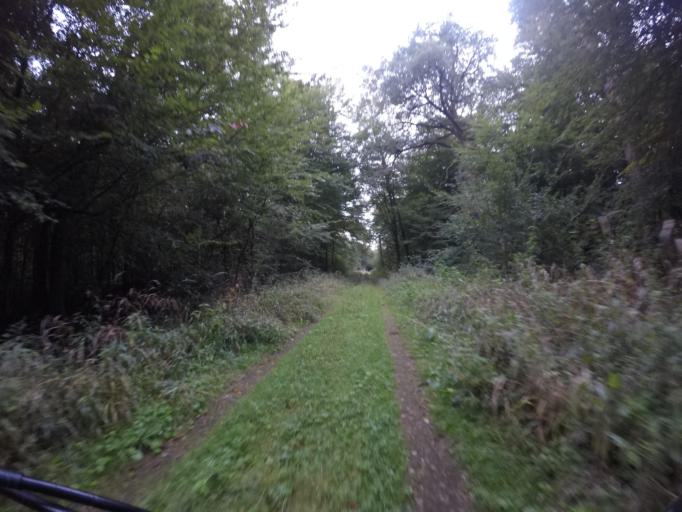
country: DE
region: Lower Saxony
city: Neu Darchau
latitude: 53.2740
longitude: 10.8915
